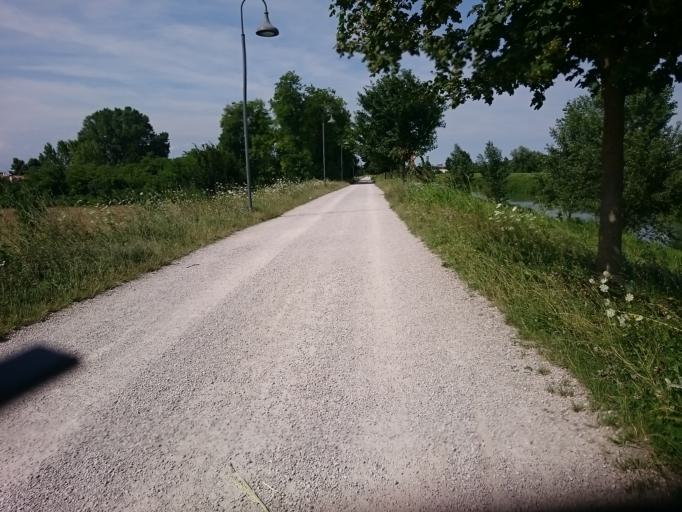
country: IT
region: Veneto
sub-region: Provincia di Padova
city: Ponte San Nicolo
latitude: 45.3896
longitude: 11.9088
